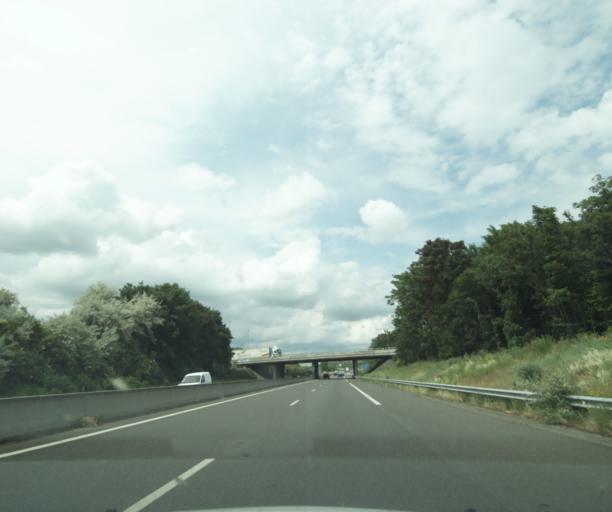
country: FR
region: Auvergne
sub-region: Departement du Puy-de-Dome
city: Perignat-les-Sarlieve
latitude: 45.7588
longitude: 3.1402
